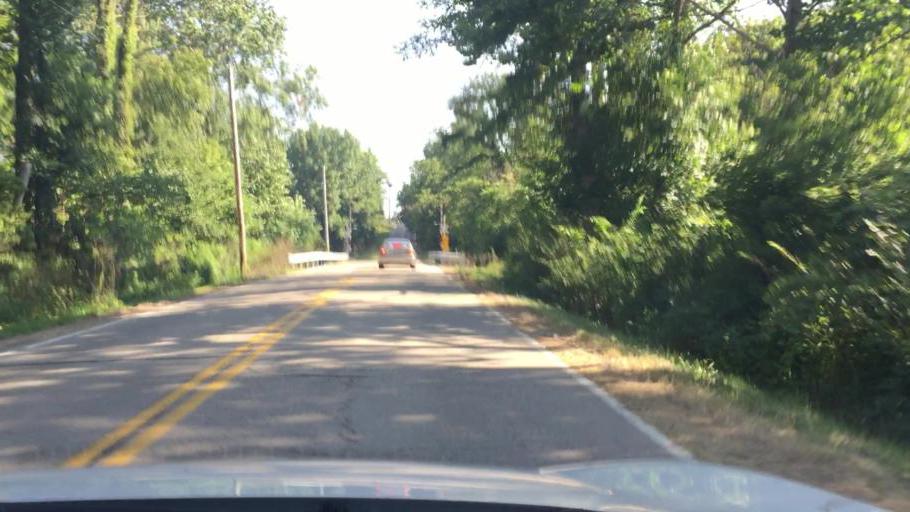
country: US
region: Ohio
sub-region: Clark County
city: Northridge
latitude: 40.0069
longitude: -83.6933
